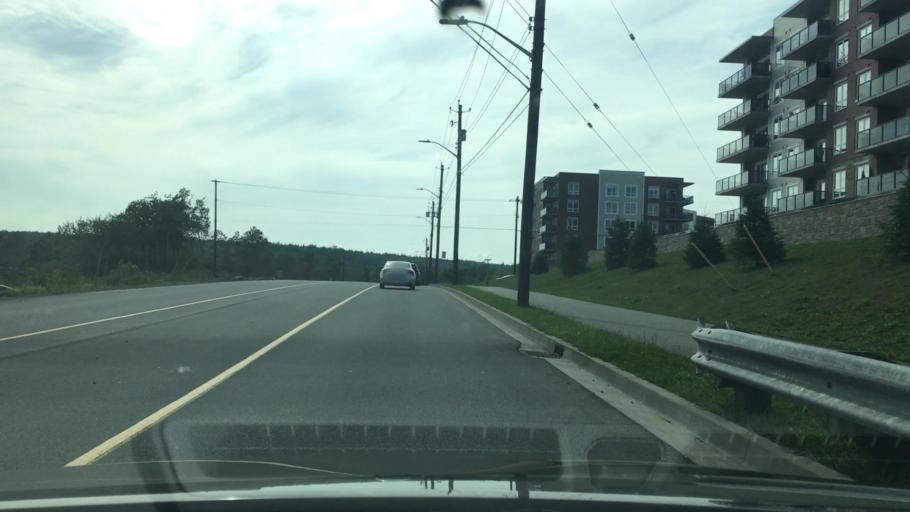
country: CA
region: Nova Scotia
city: Dartmouth
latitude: 44.6997
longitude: -63.6965
